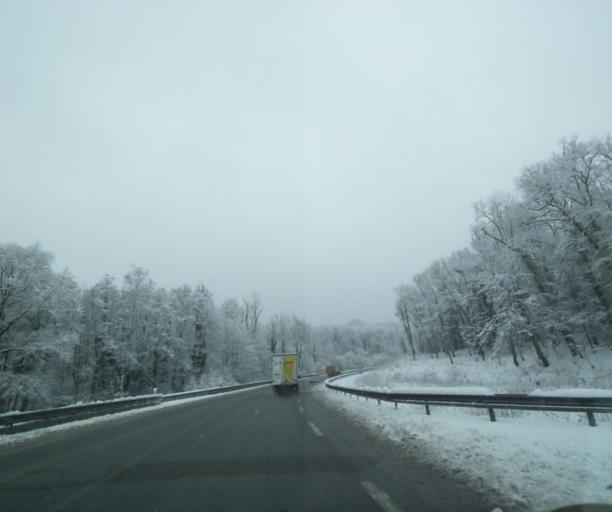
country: FR
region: Champagne-Ardenne
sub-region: Departement de la Haute-Marne
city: Saint-Dizier
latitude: 48.6148
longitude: 4.9180
